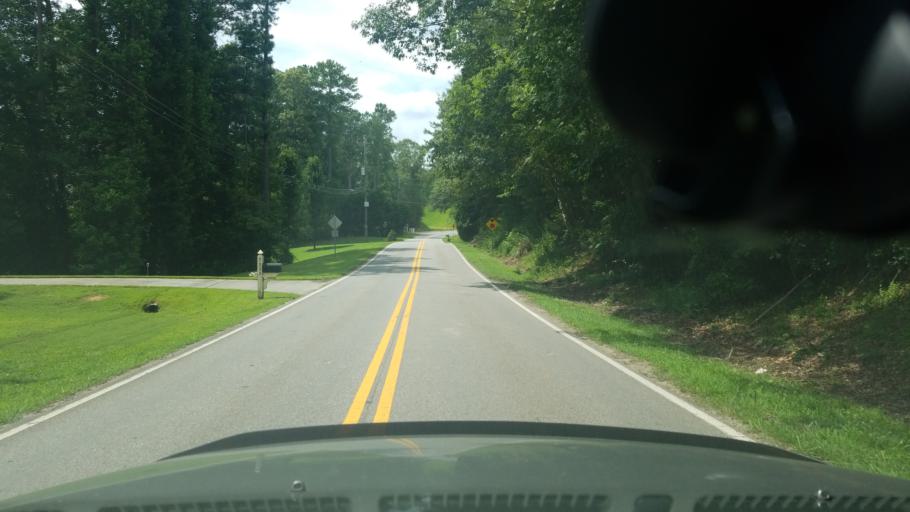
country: US
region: Georgia
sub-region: Forsyth County
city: Cumming
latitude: 34.2960
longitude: -84.2390
